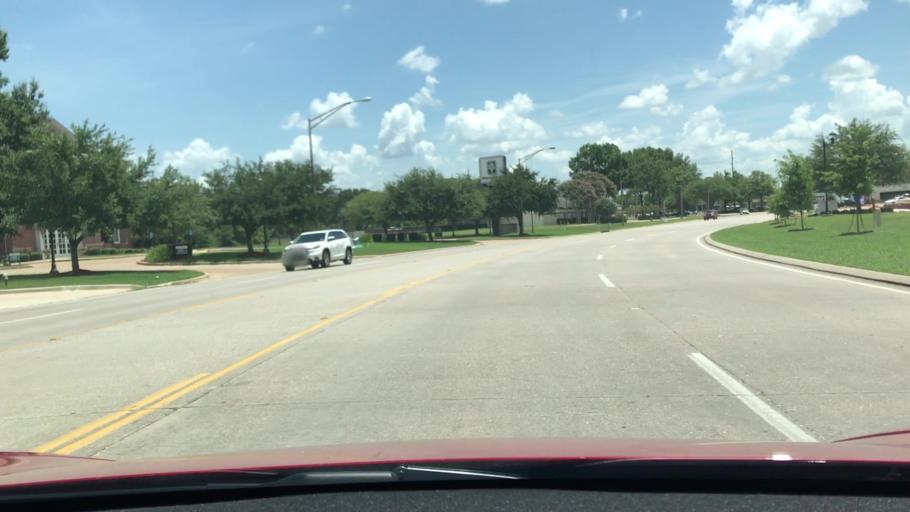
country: US
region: Louisiana
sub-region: Bossier Parish
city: Bossier City
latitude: 32.4253
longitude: -93.7227
